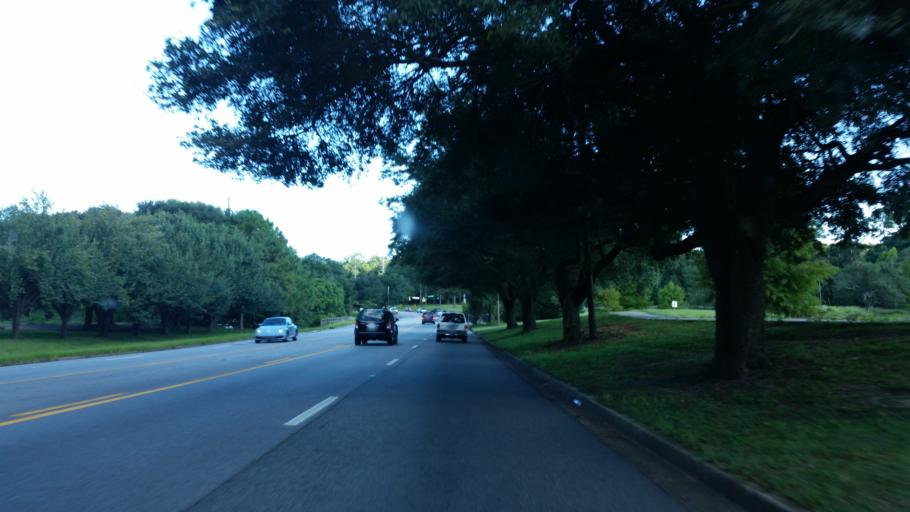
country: US
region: Alabama
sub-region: Mobile County
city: Prichard
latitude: 30.7072
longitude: -88.1522
